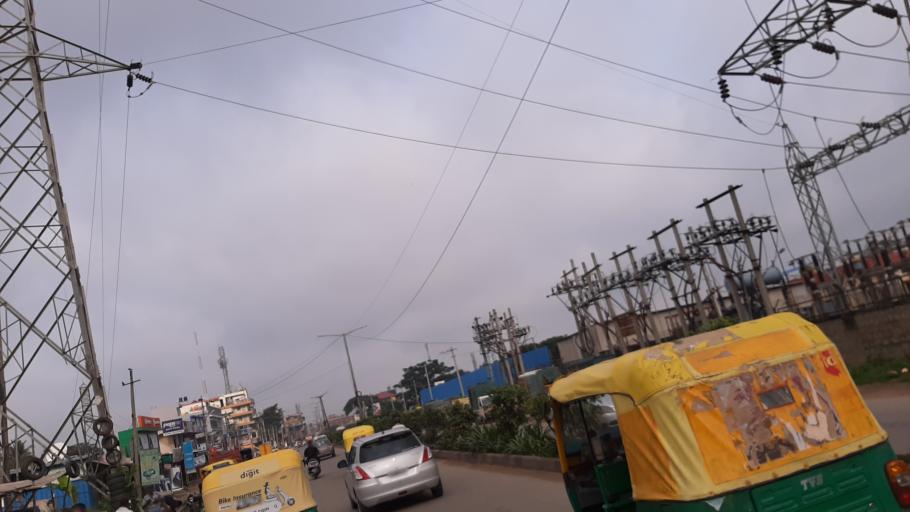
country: IN
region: Karnataka
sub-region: Bangalore Urban
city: Bangalore
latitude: 12.9852
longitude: 77.4815
